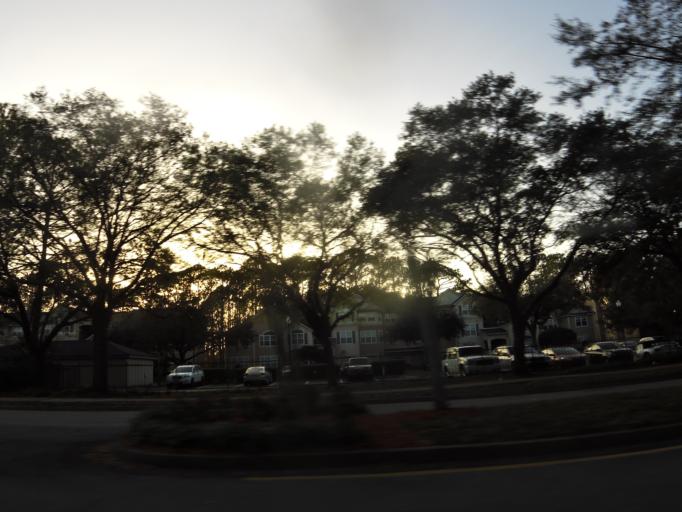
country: US
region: Florida
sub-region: Duval County
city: Jacksonville Beach
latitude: 30.2618
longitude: -81.4598
